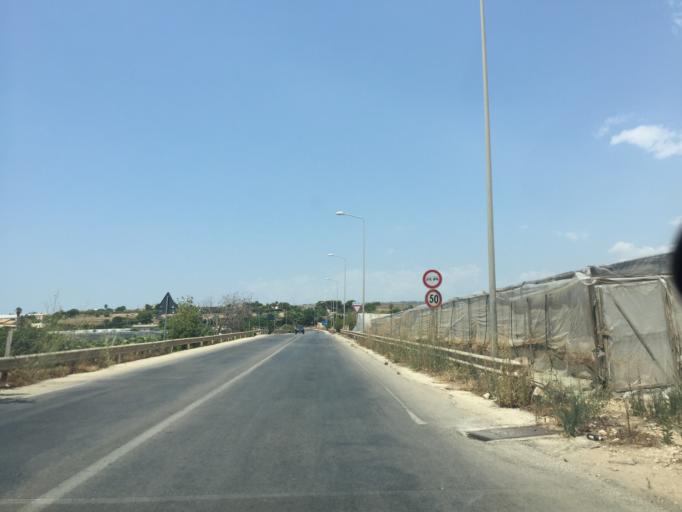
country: IT
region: Sicily
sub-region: Ragusa
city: Donnalucata
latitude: 36.7736
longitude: 14.6090
